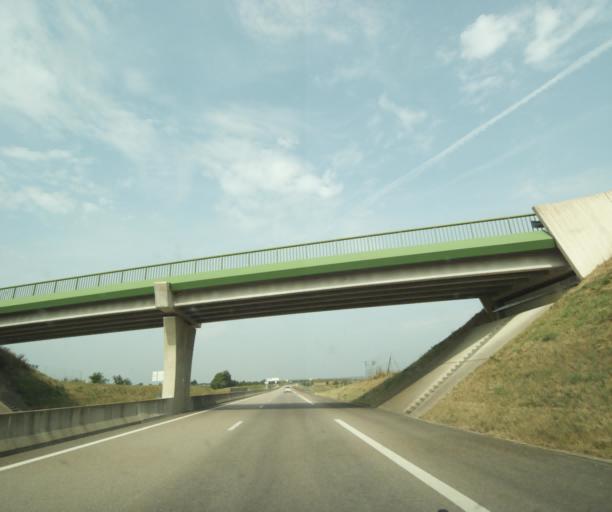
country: FR
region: Lower Normandy
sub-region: Departement du Calvados
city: Falaise
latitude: 48.8702
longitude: -0.2081
